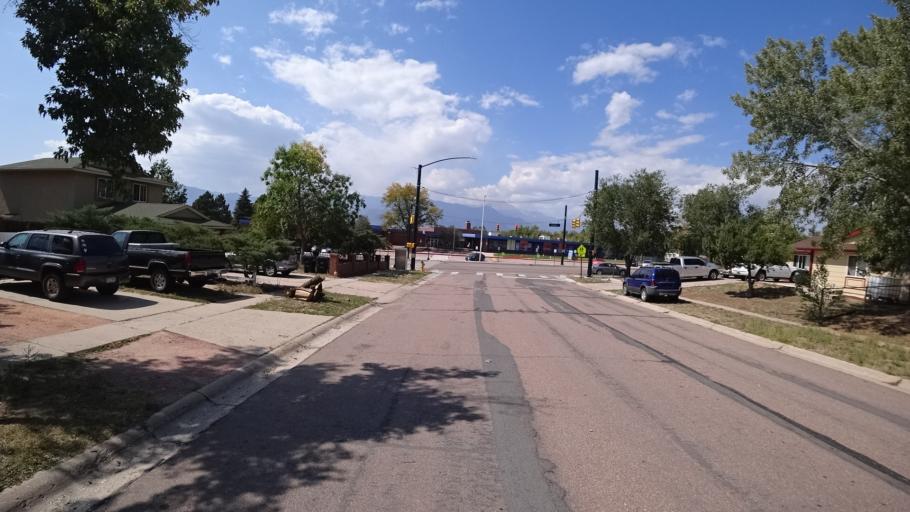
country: US
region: Colorado
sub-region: El Paso County
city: Colorado Springs
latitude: 38.8297
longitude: -104.7754
